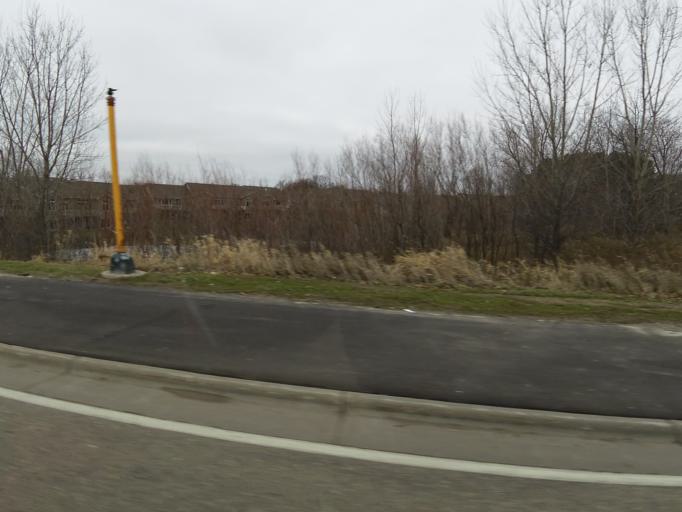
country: US
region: Minnesota
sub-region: Scott County
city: Prior Lake
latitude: 44.7276
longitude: -93.4395
